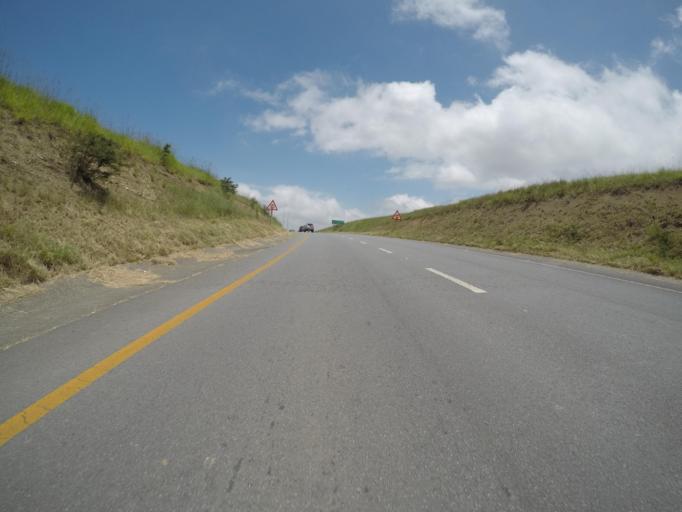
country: ZA
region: Eastern Cape
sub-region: Buffalo City Metropolitan Municipality
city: East London
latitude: -32.9505
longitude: 27.9337
